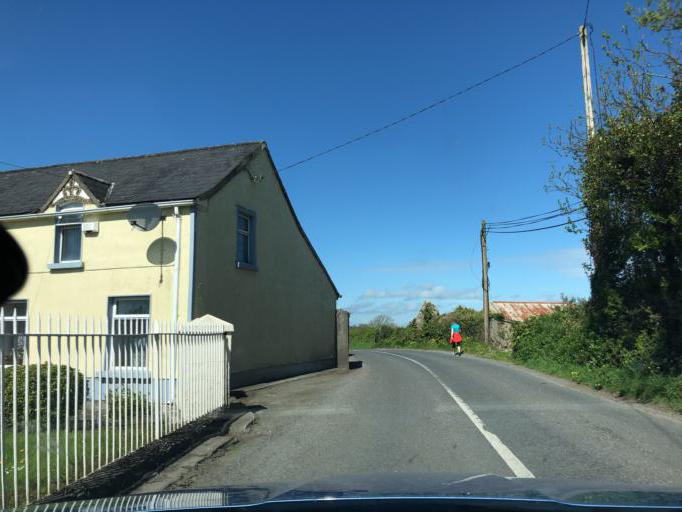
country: IE
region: Connaught
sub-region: County Galway
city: Portumna
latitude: 53.1572
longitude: -8.3879
